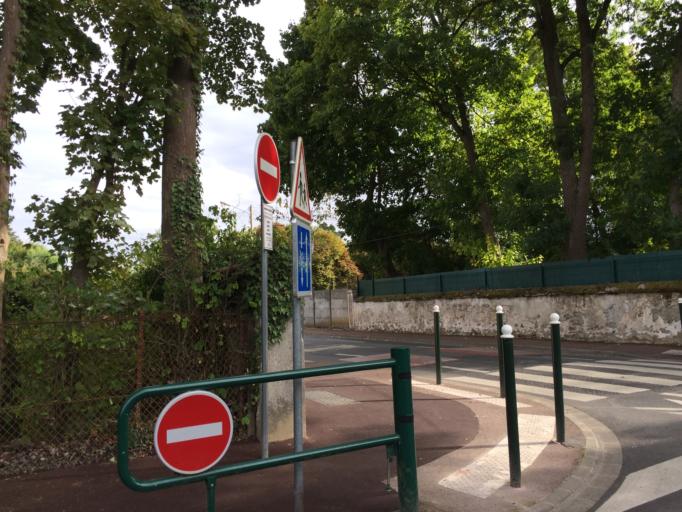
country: FR
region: Ile-de-France
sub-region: Departement de l'Essonne
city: Soisy-sur-Seine
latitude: 48.6477
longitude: 2.4441
